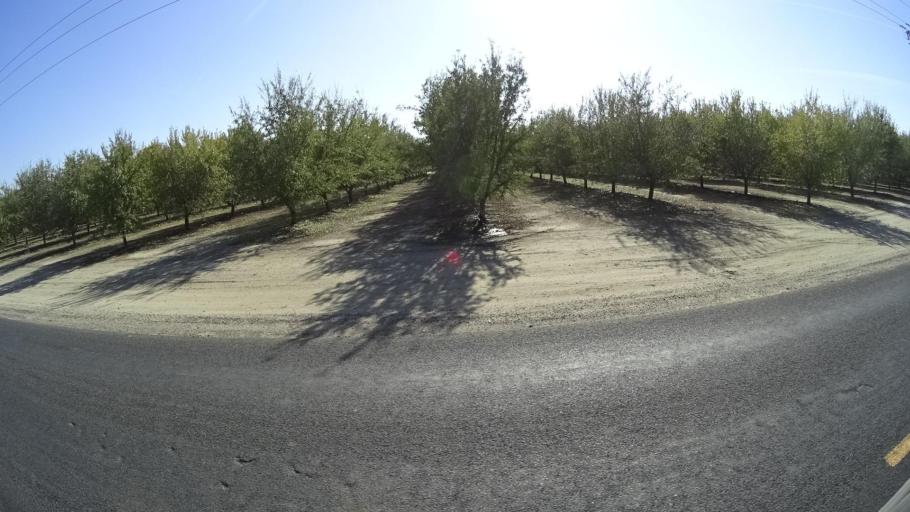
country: US
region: California
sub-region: Kern County
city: McFarland
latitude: 35.6453
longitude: -119.2742
